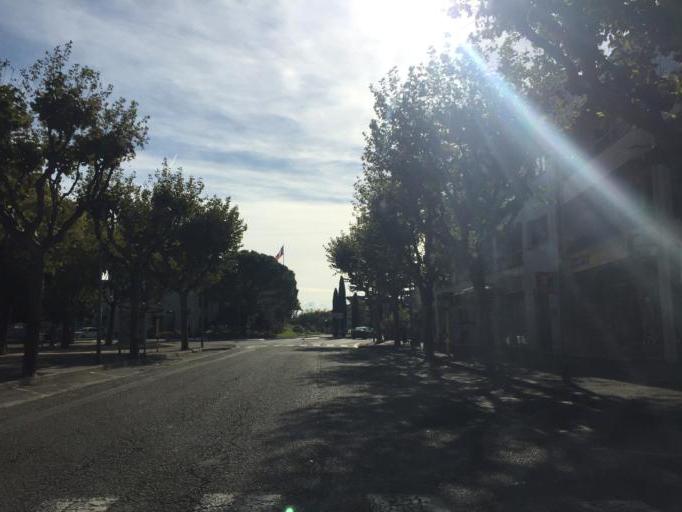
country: FR
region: Rhone-Alpes
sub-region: Departement de la Drome
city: Pierrelatte
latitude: 44.3769
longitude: 4.6994
